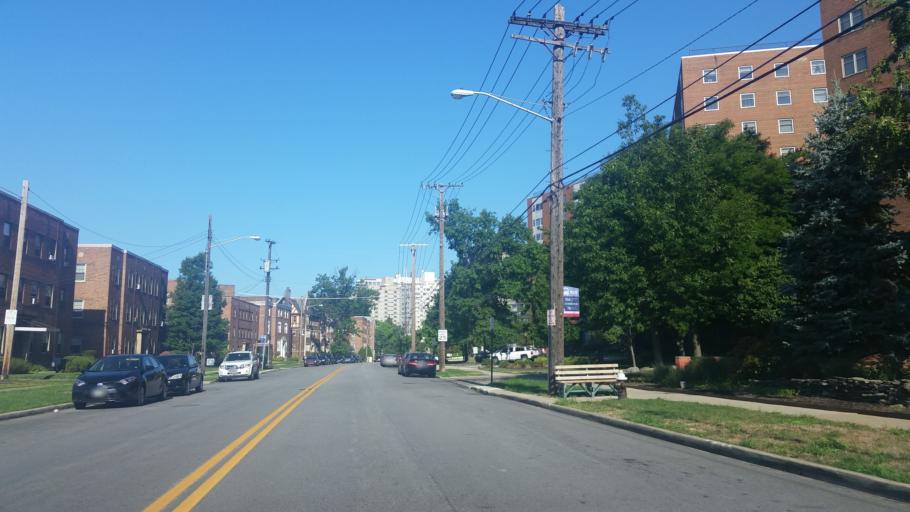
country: US
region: Ohio
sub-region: Cuyahoga County
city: Lakewood
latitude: 41.4905
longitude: -81.7707
